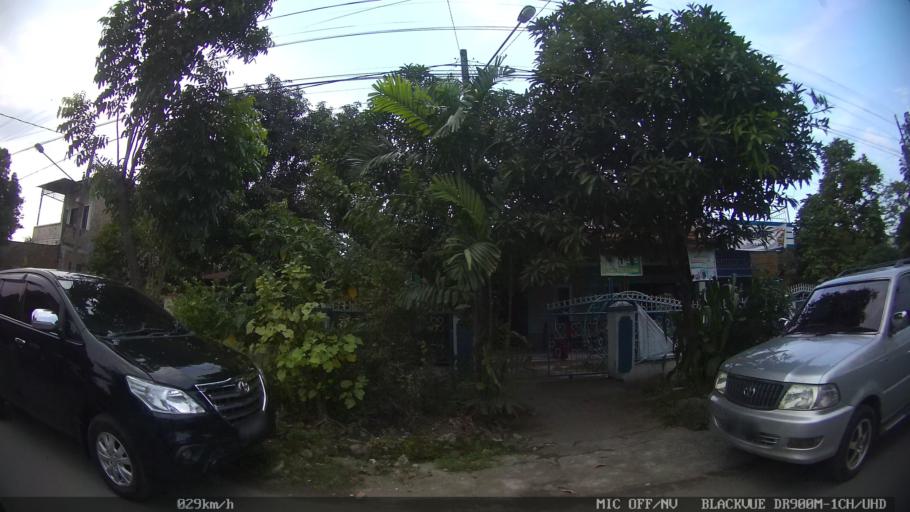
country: ID
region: North Sumatra
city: Medan
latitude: 3.6099
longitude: 98.6865
